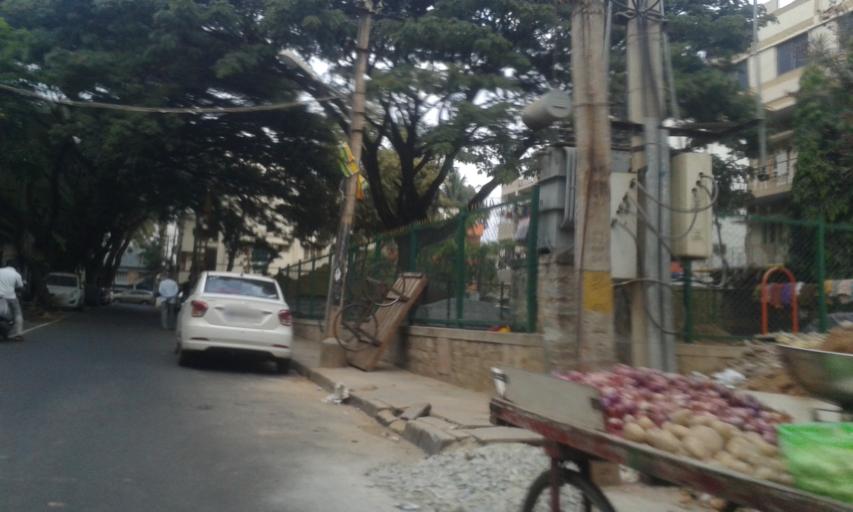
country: IN
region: Karnataka
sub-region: Bangalore Urban
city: Bangalore
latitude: 12.9346
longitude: 77.5912
